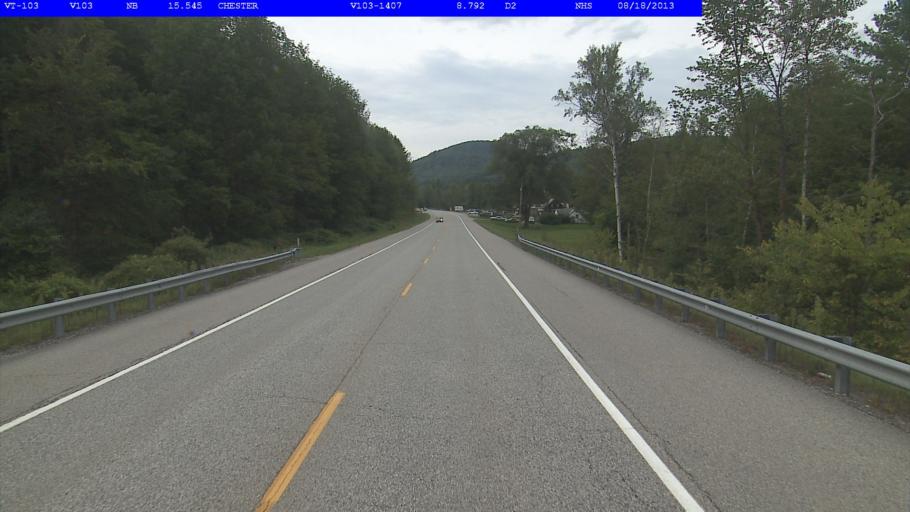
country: US
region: Vermont
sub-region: Windsor County
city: Chester
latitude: 43.3373
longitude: -72.6174
